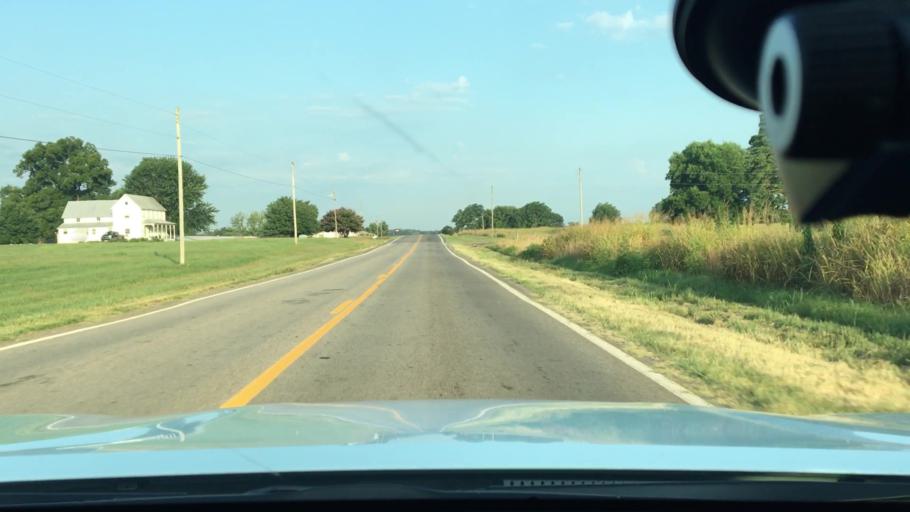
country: US
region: Arkansas
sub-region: Johnson County
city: Clarksville
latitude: 35.3789
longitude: -93.5423
